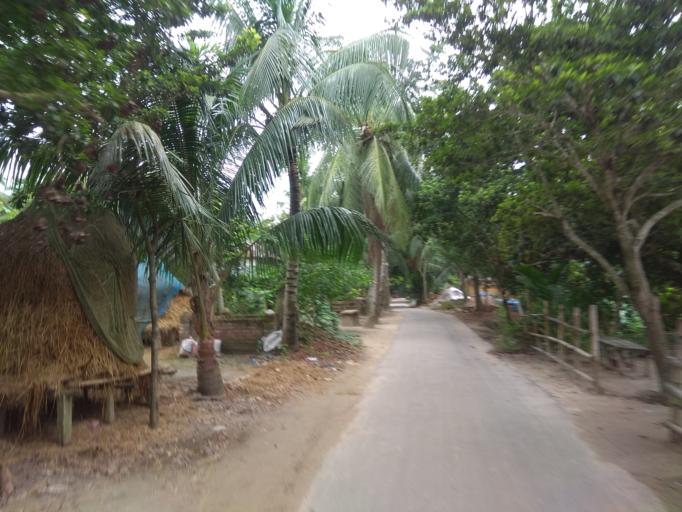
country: BD
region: Dhaka
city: Dohar
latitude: 23.4839
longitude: 90.0036
